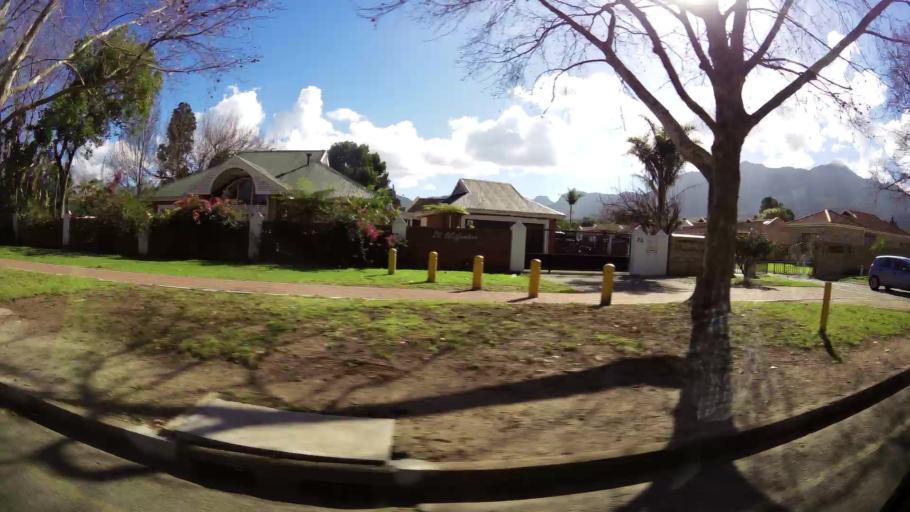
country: ZA
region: Western Cape
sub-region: Eden District Municipality
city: George
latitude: -33.9511
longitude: 22.4293
